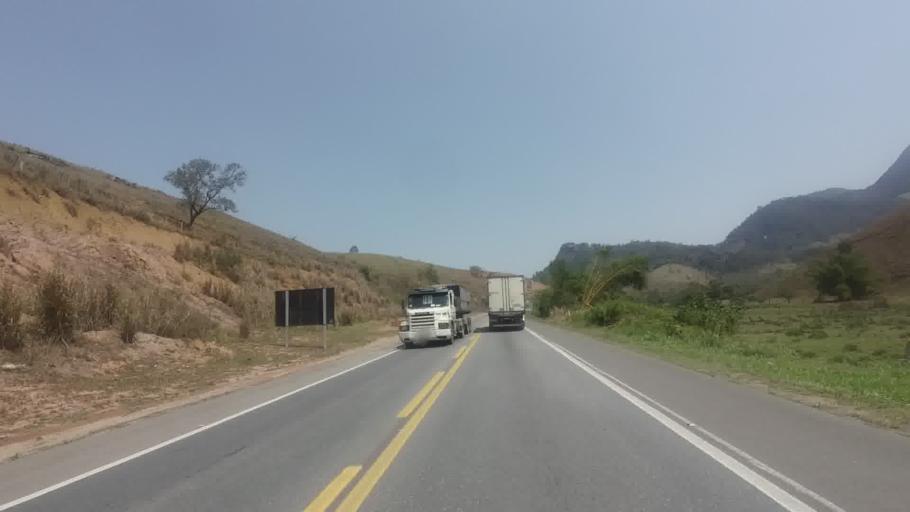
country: BR
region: Espirito Santo
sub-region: Rio Novo Do Sul
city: Rio Novo do Sul
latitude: -20.8807
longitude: -40.9702
